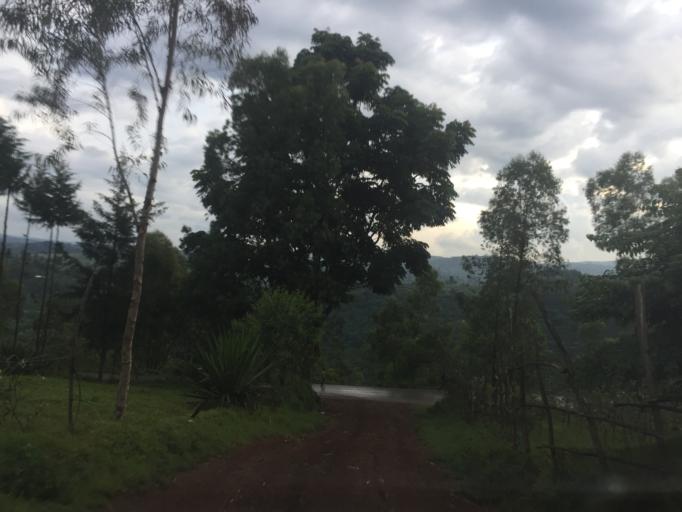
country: CD
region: South Kivu
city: Kabare
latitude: -2.4017
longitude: 28.8053
